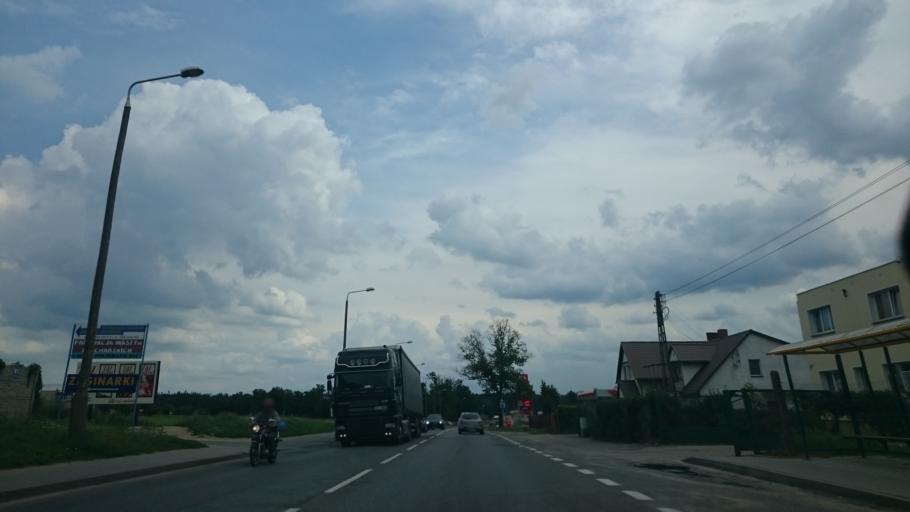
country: PL
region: Kujawsko-Pomorskie
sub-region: Powiat tucholski
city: Tuchola
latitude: 53.5800
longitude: 17.8739
